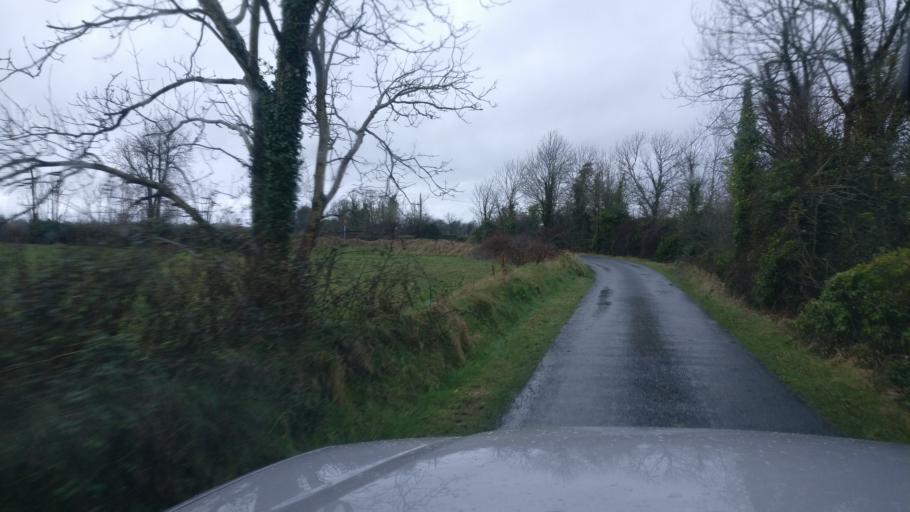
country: IE
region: Connaught
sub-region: County Galway
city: Ballinasloe
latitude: 53.2470
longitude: -8.3544
